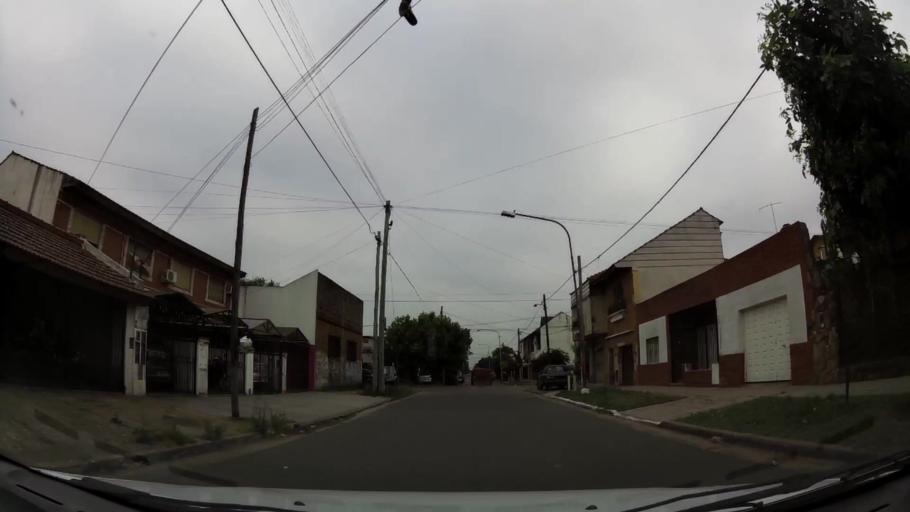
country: AR
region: Buenos Aires
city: San Justo
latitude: -34.6972
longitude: -58.5664
